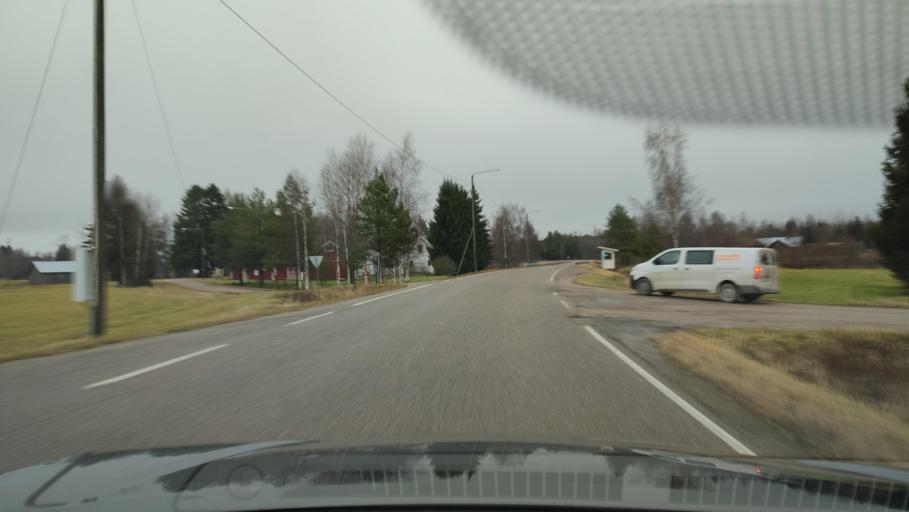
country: FI
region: Southern Ostrobothnia
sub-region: Suupohja
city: Isojoki
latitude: 62.2350
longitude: 22.0230
